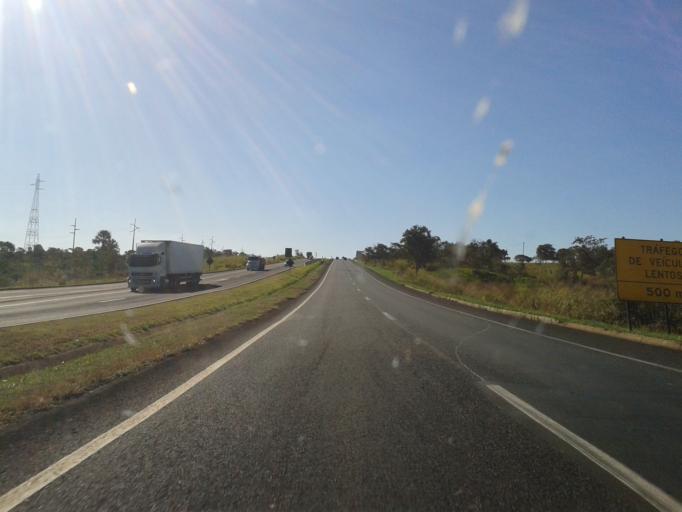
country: BR
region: Minas Gerais
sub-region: Uberlandia
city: Uberlandia
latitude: -19.1576
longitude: -48.1643
